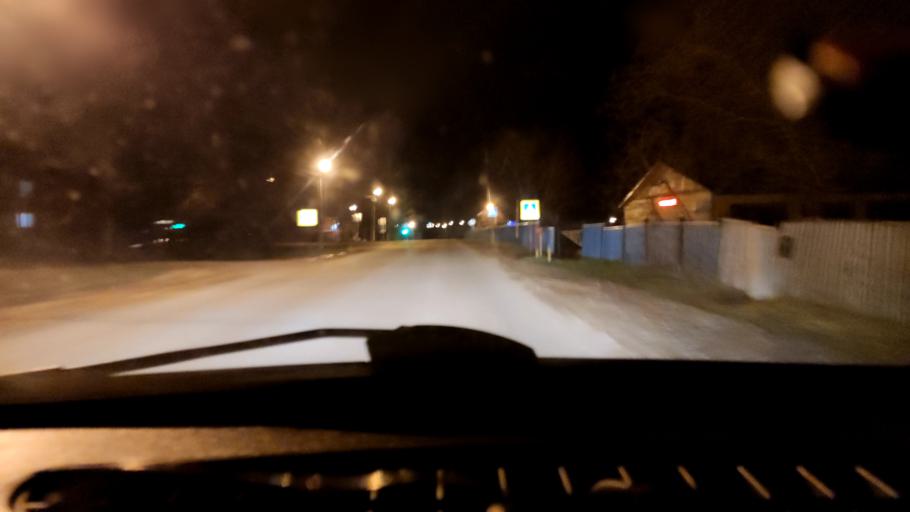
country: RU
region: Bashkortostan
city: Karmaskaly
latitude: 54.3667
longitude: 56.1729
